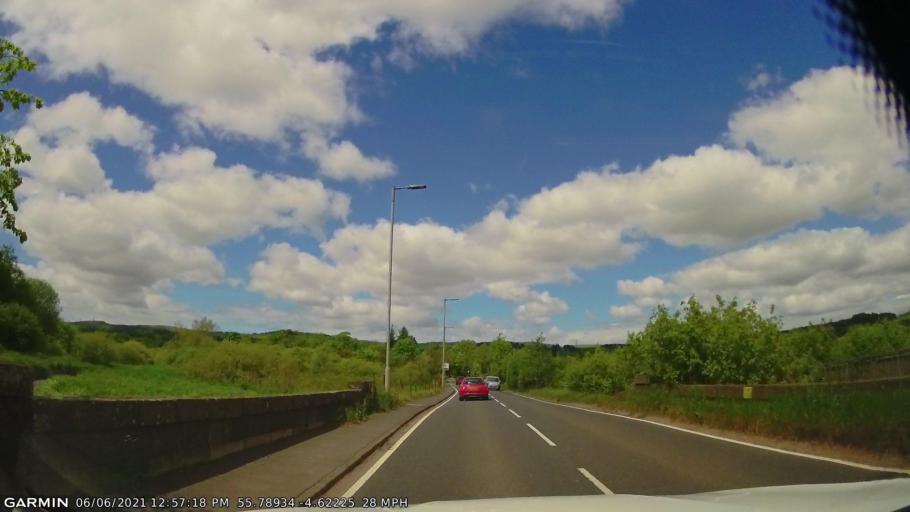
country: GB
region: Scotland
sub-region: Renfrewshire
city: Lochwinnoch
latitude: 55.7893
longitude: -4.6223
